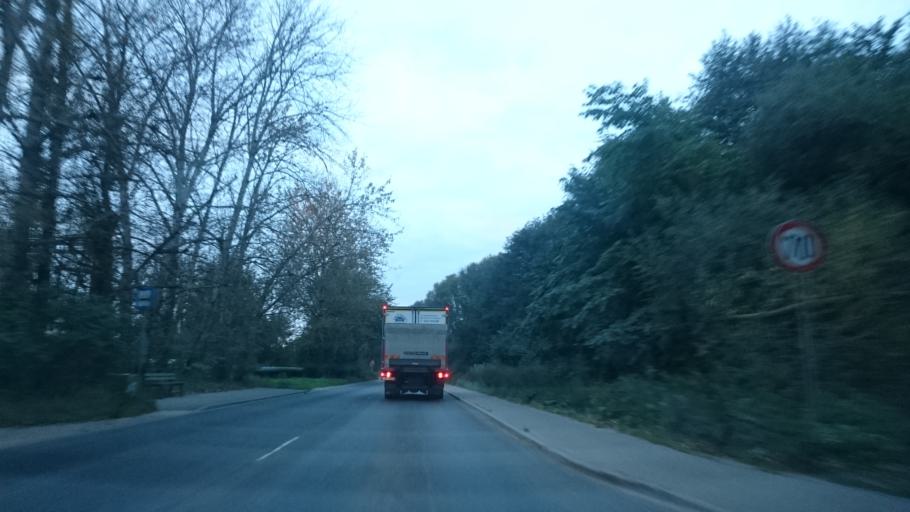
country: LV
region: Kekava
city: Balozi
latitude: 56.9150
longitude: 24.2006
